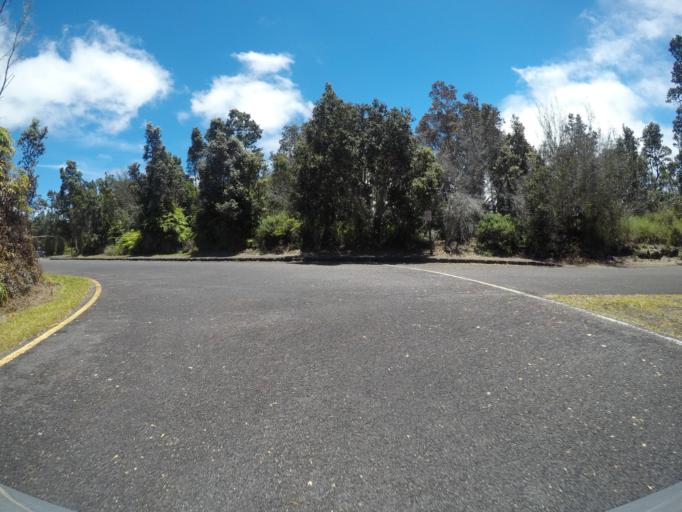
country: US
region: Hawaii
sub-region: Hawaii County
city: Volcano
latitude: 19.3650
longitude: -155.2156
